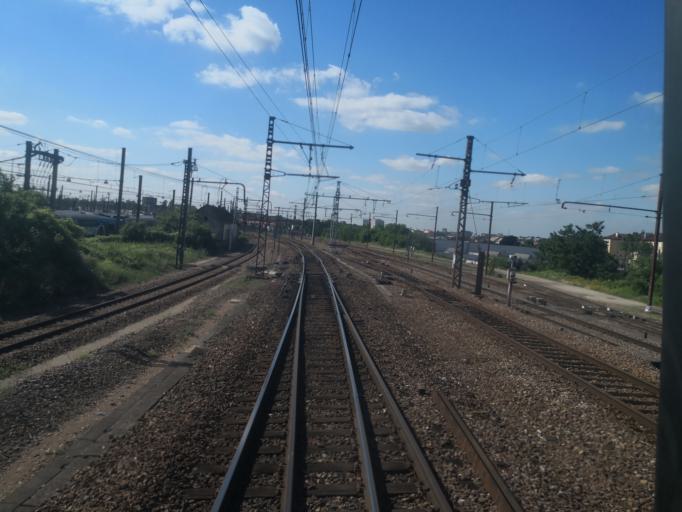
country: FR
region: Ile-de-France
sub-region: Departement de Seine-et-Marne
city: Melun
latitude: 48.5234
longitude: 2.6641
